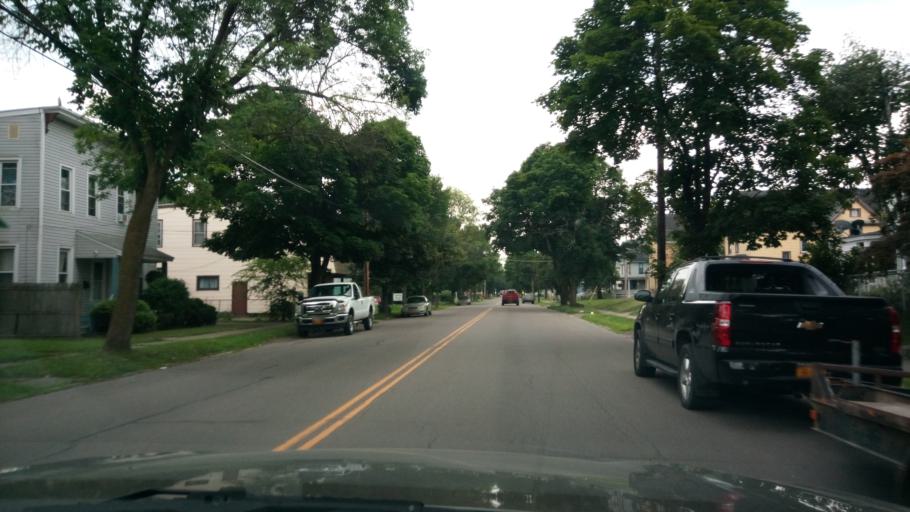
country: US
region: New York
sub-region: Chemung County
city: Elmira
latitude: 42.1065
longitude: -76.8054
